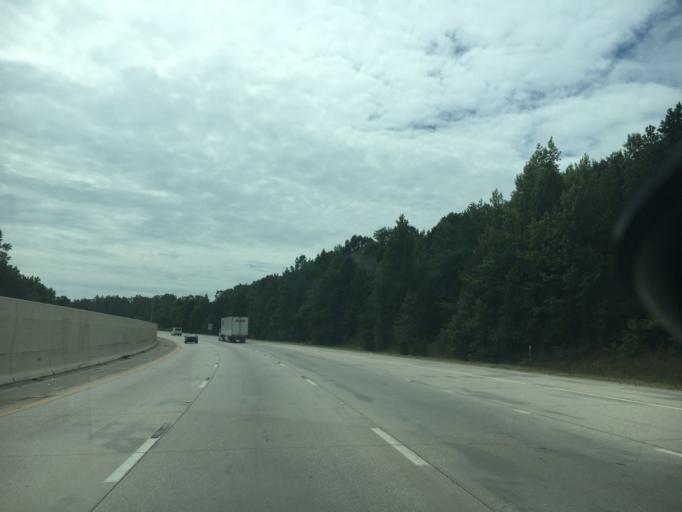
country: US
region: South Carolina
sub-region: Greenville County
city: Mauldin
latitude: 34.7863
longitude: -82.2812
